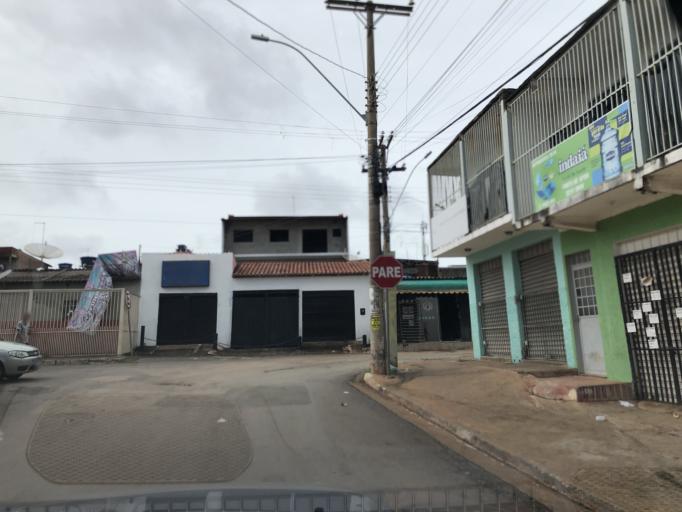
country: BR
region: Federal District
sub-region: Brasilia
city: Brasilia
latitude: -15.7842
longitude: -48.1392
